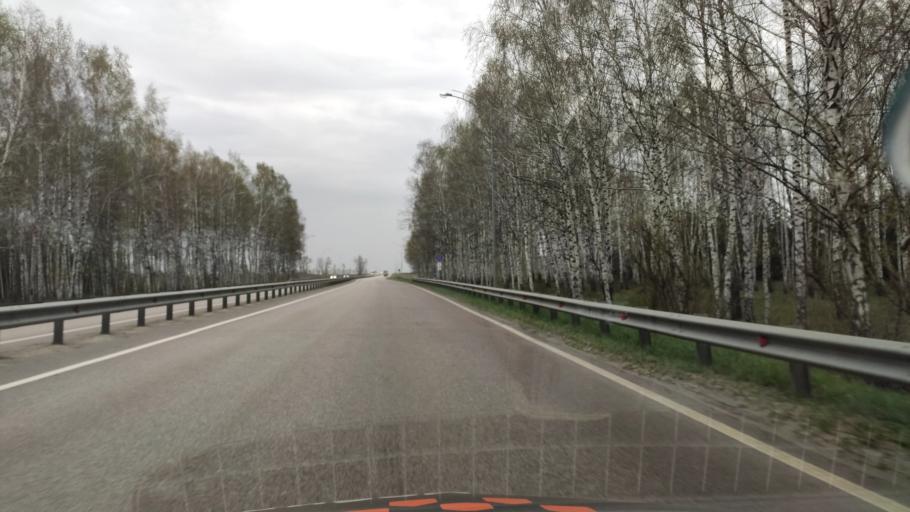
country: RU
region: Belgorod
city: Staryy Oskol
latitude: 51.4103
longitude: 37.8832
